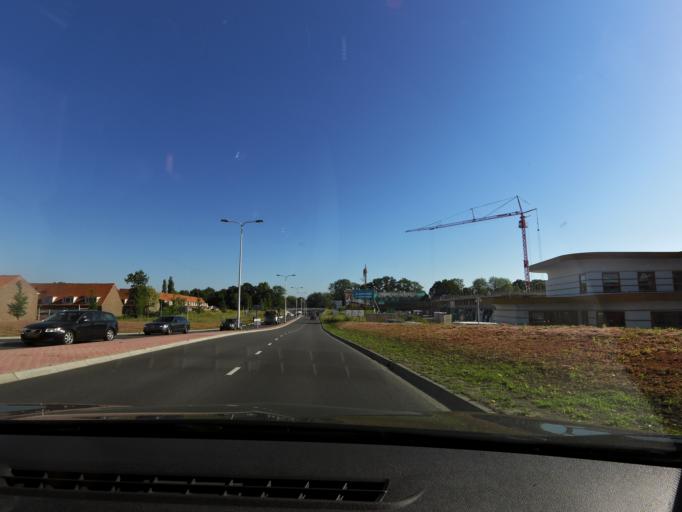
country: NL
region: Overijssel
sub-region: Gemeente Deventer
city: Deventer
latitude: 52.2543
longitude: 6.1807
